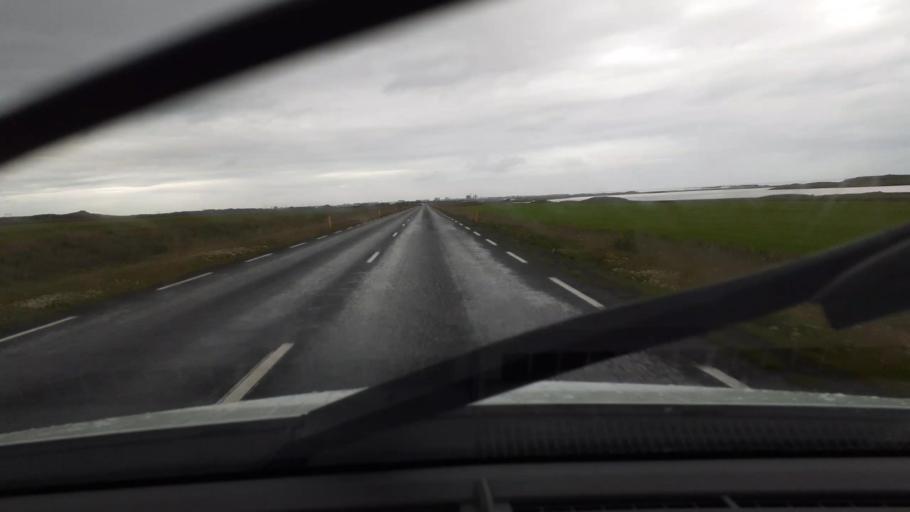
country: IS
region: West
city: Akranes
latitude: 64.3520
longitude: -21.9941
